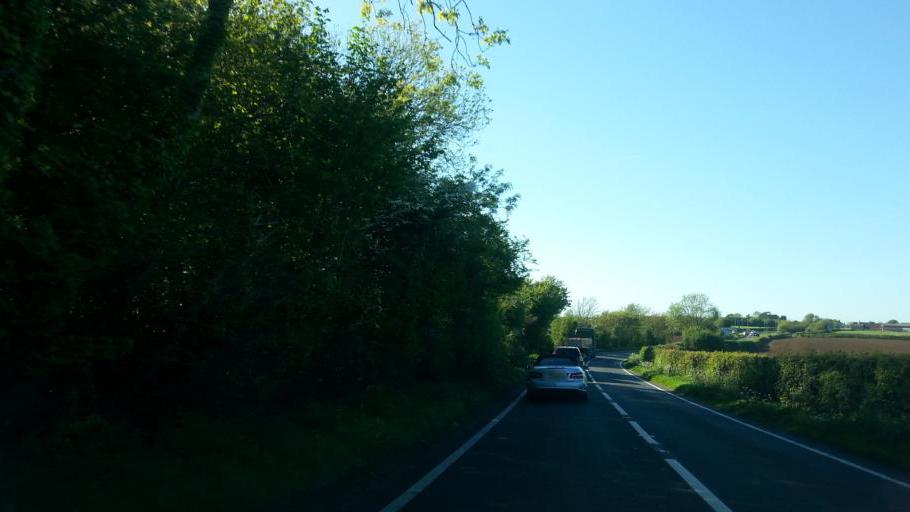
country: GB
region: England
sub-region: Somerset
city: Shepton Mallet
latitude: 51.1668
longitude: -2.5322
